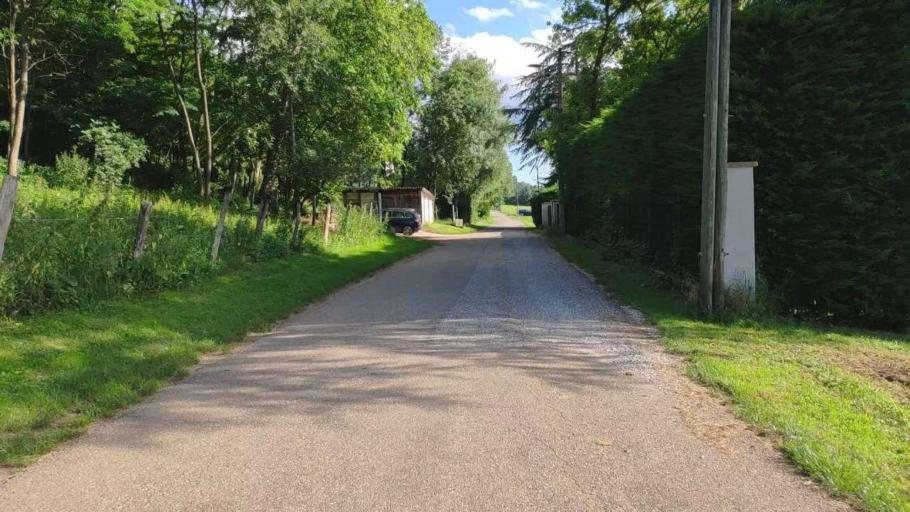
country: FR
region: Franche-Comte
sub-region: Departement du Jura
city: Bletterans
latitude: 46.7574
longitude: 5.5229
